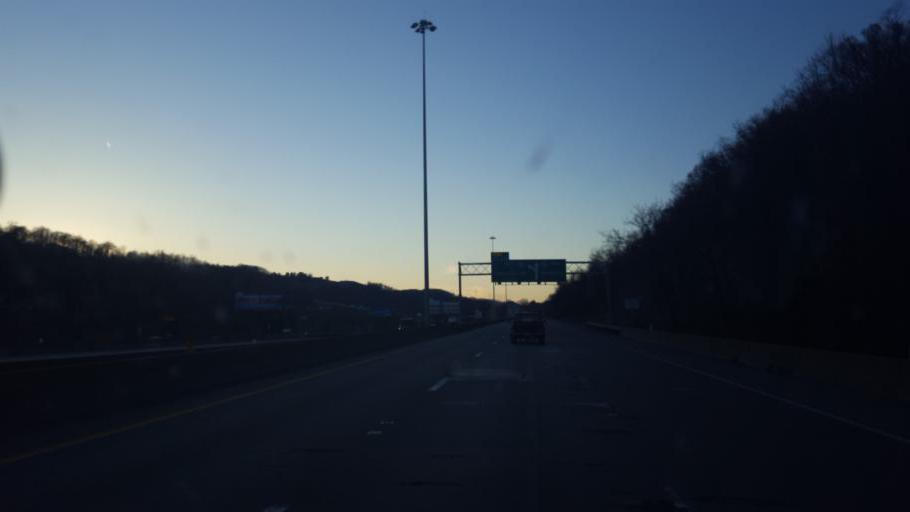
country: US
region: West Virginia
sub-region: Ohio County
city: Bethlehem
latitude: 40.0454
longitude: -80.6567
